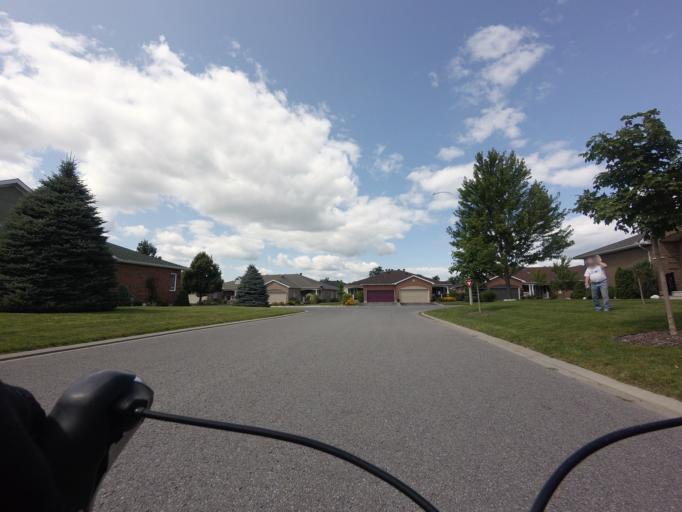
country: CA
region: Ontario
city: Bells Corners
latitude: 45.2938
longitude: -75.8482
